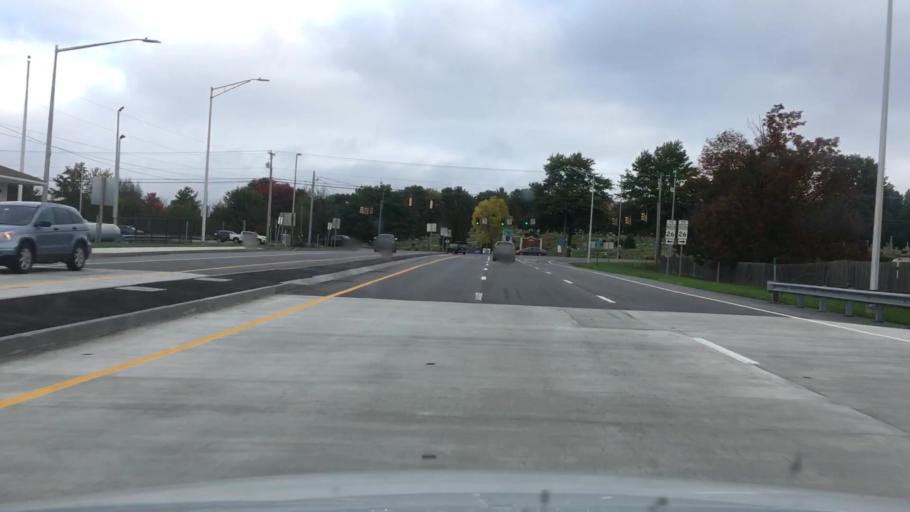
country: US
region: Maine
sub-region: Cumberland County
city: New Gloucester
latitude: 43.8829
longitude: -70.3331
